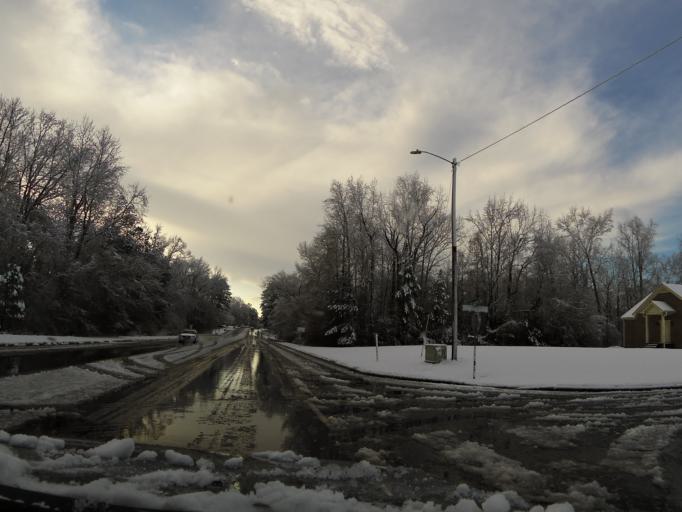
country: US
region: North Carolina
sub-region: Nash County
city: Rocky Mount
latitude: 35.9428
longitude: -77.8492
